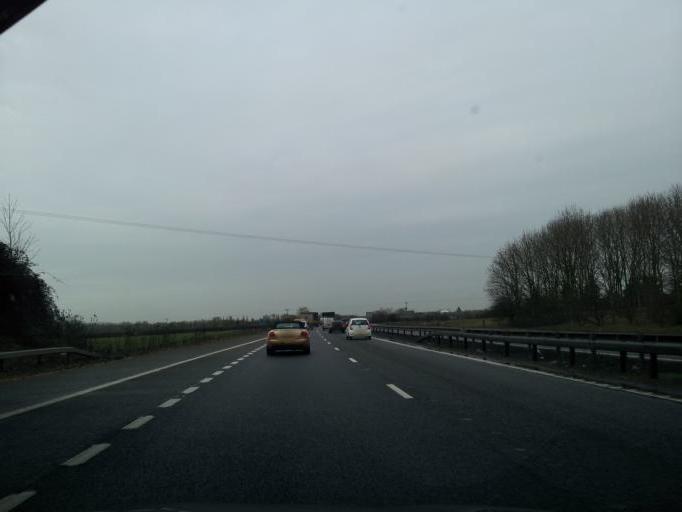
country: GB
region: England
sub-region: Cambridgeshire
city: Barton
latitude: 52.1933
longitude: 0.0740
